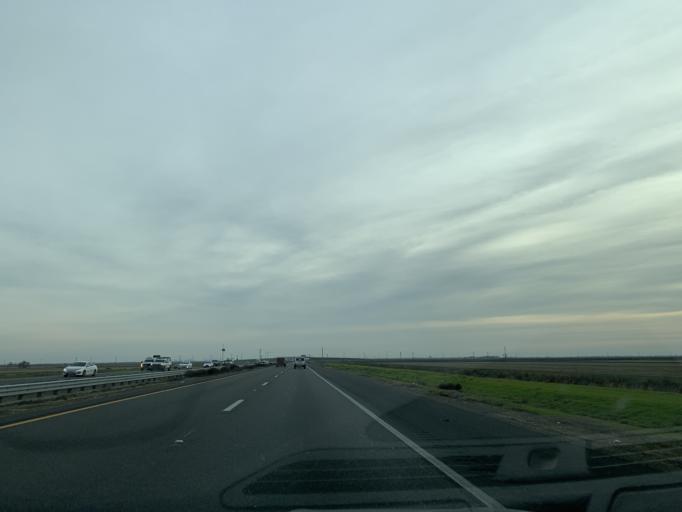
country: US
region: California
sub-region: Sacramento County
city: Elverta
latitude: 38.7264
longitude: -121.5406
